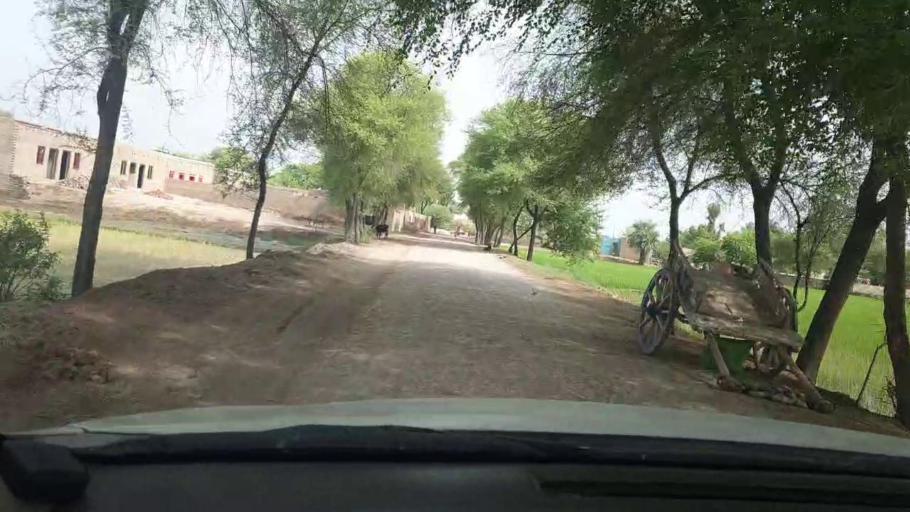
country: PK
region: Sindh
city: Shikarpur
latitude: 28.0035
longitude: 68.5933
